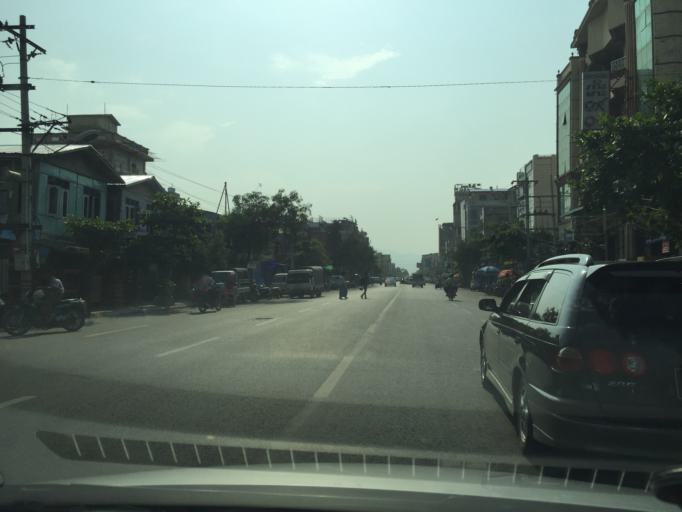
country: MM
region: Mandalay
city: Mandalay
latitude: 21.9689
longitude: 96.0900
